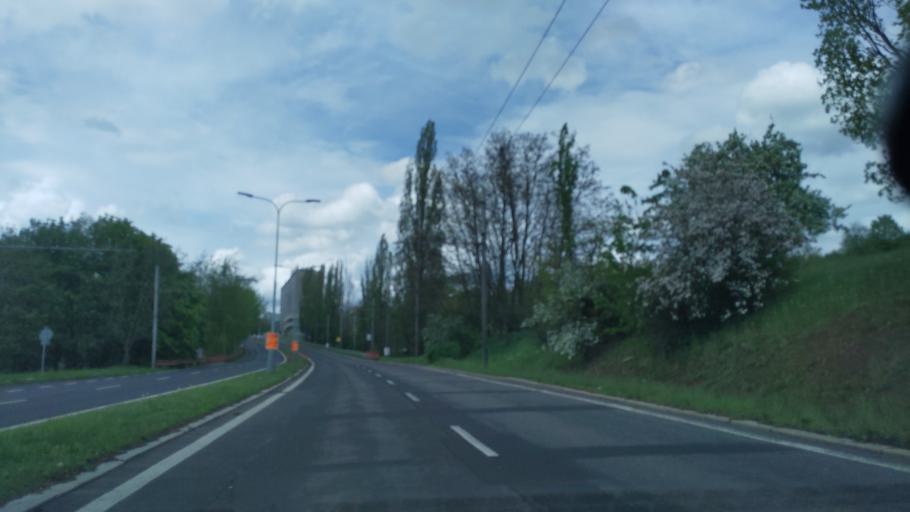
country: CZ
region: Ustecky
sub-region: Okres Usti nad Labem
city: Usti nad Labem
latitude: 50.6730
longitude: 14.0332
